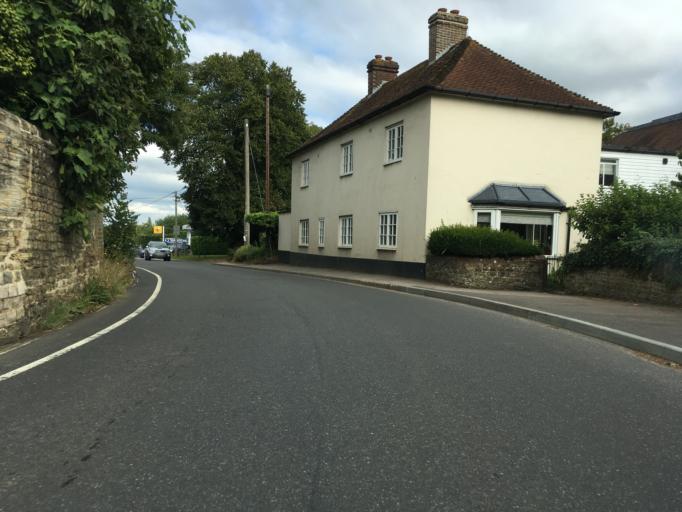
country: GB
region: England
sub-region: West Sussex
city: Milland
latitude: 51.0081
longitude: -0.8496
